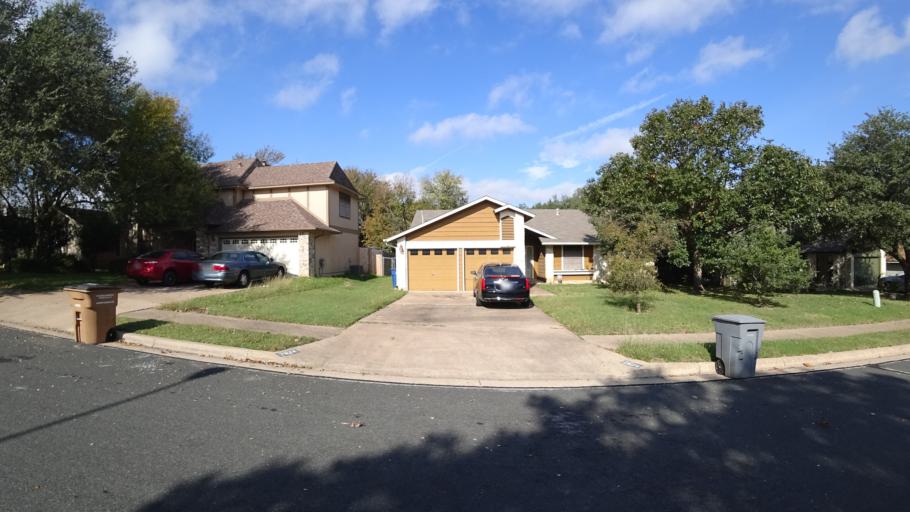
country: US
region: Texas
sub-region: Travis County
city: Shady Hollow
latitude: 30.1955
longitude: -97.8267
